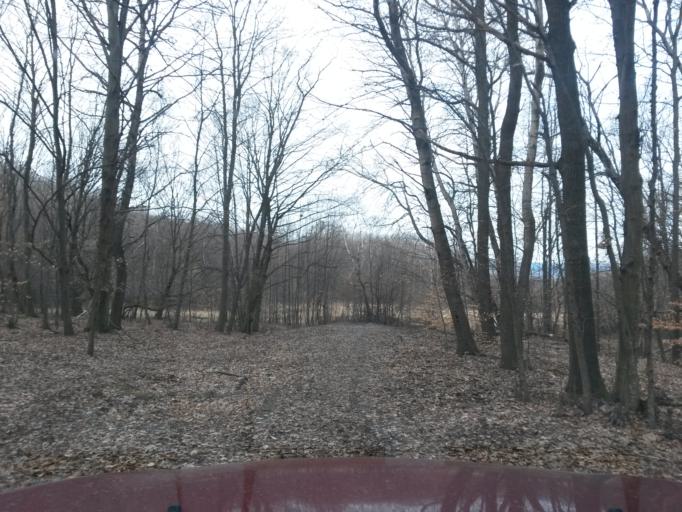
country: HU
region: Borsod-Abauj-Zemplen
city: Gonc
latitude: 48.5738
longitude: 21.3899
